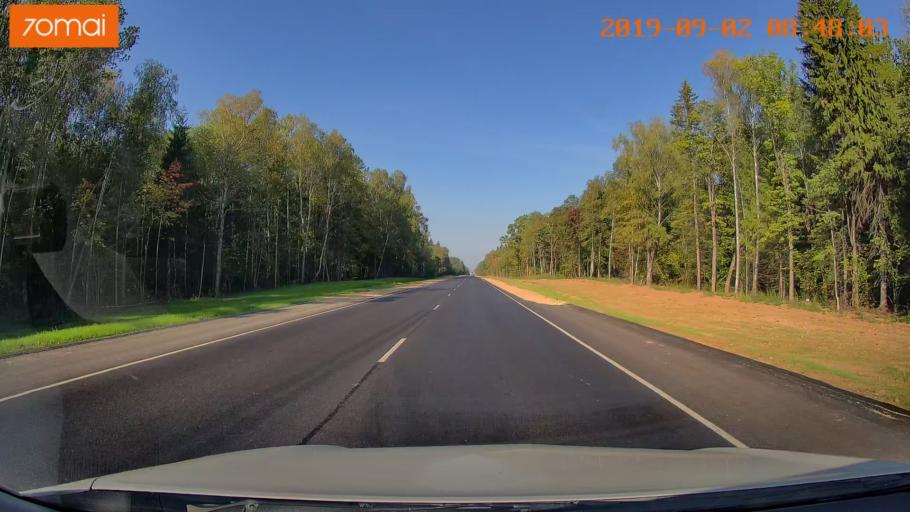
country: RU
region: Kaluga
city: Medyn'
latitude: 54.9674
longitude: 35.9419
